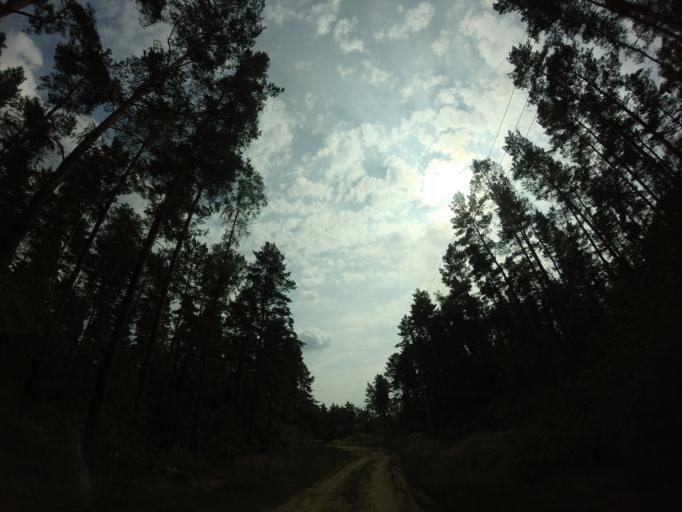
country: PL
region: West Pomeranian Voivodeship
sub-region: Powiat drawski
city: Drawsko Pomorskie
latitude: 53.4603
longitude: 15.7361
